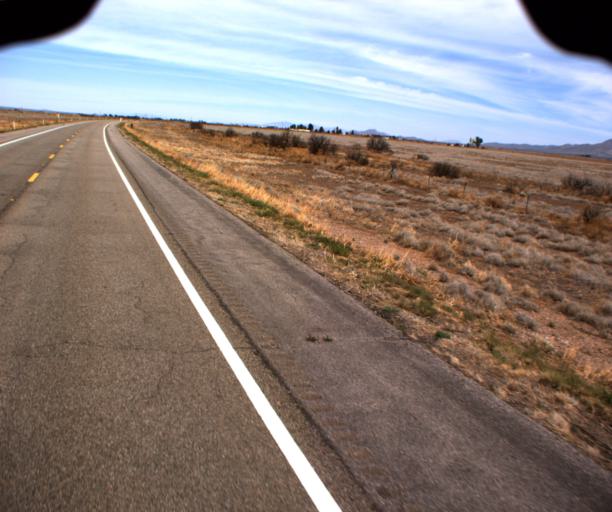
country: US
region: Arizona
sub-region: Cochise County
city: Pirtleville
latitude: 31.5604
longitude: -109.6667
